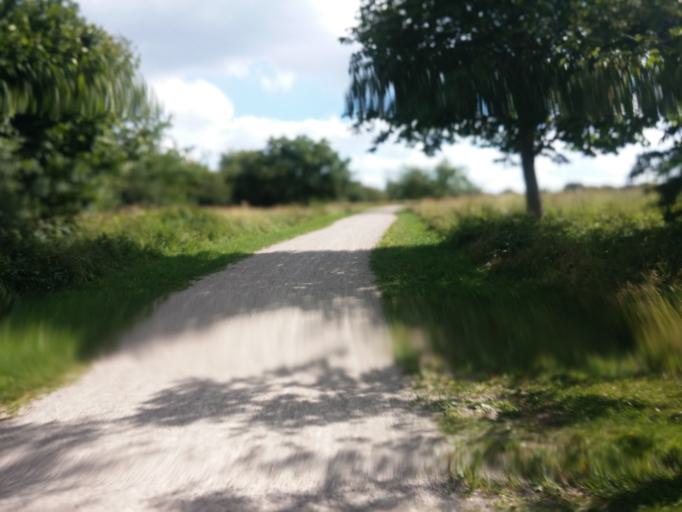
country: DE
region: Bavaria
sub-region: Upper Bavaria
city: Unterfoehring
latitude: 48.1494
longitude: 11.6639
